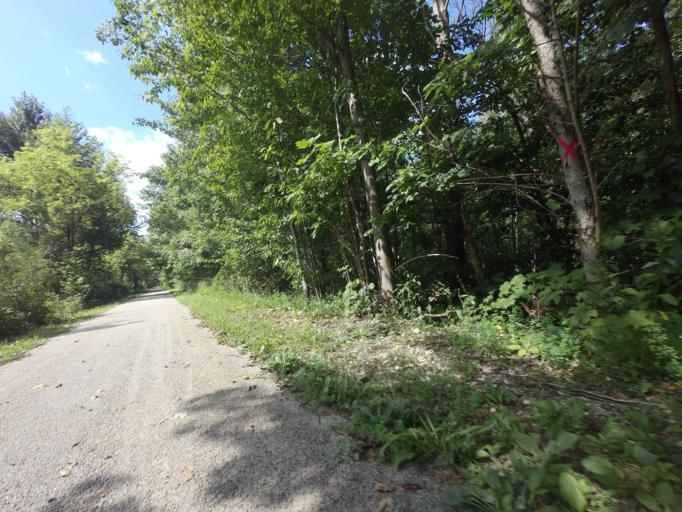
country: CA
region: Ontario
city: Huron East
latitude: 43.6752
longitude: -81.2873
